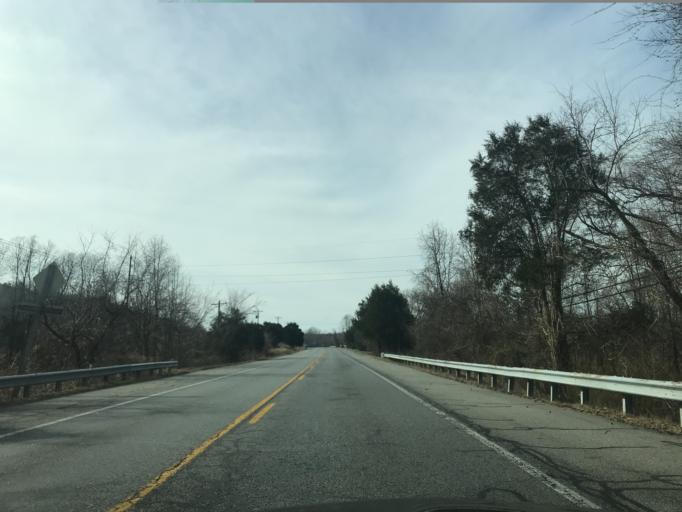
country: US
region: Maryland
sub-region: Charles County
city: La Plata
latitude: 38.5210
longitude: -77.0137
